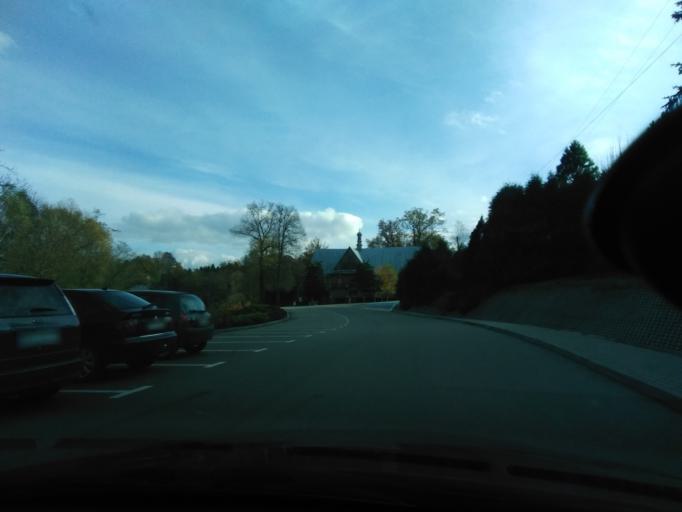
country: PL
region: Subcarpathian Voivodeship
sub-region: Powiat ropczycko-sedziszowski
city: Wielopole Skrzynskie
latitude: 49.9306
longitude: 21.5523
